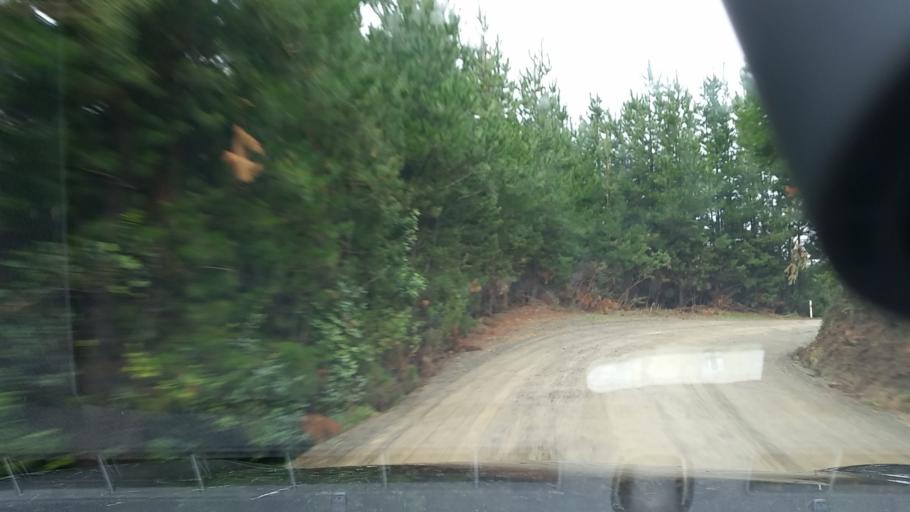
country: NZ
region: Marlborough
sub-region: Marlborough District
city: Picton
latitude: -41.3670
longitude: 174.0702
